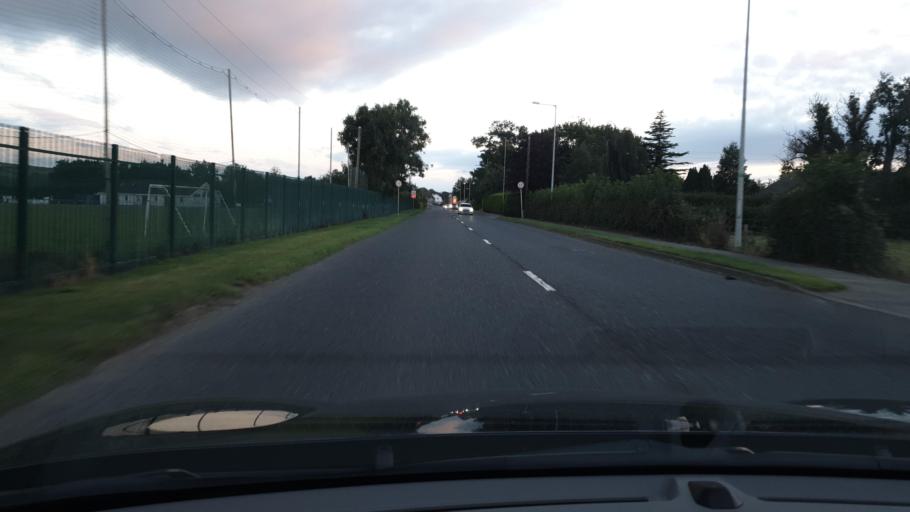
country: IE
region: Leinster
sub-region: An Mhi
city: Duleek
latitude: 53.6700
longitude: -6.3960
